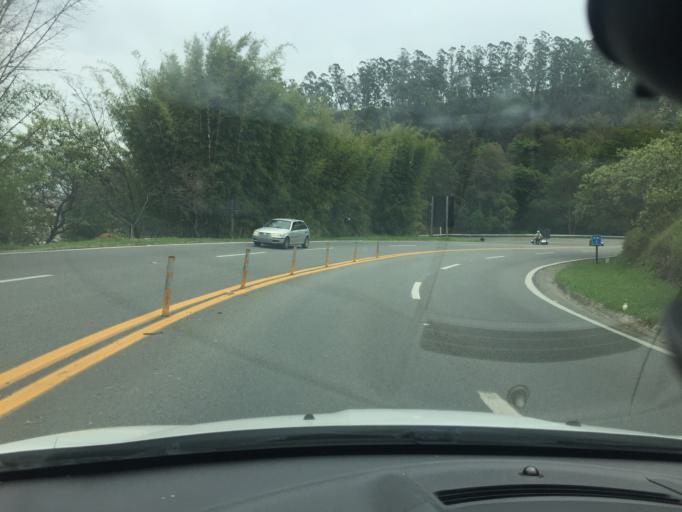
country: BR
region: Sao Paulo
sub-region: Jundiai
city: Jundiai
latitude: -23.1703
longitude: -46.8807
